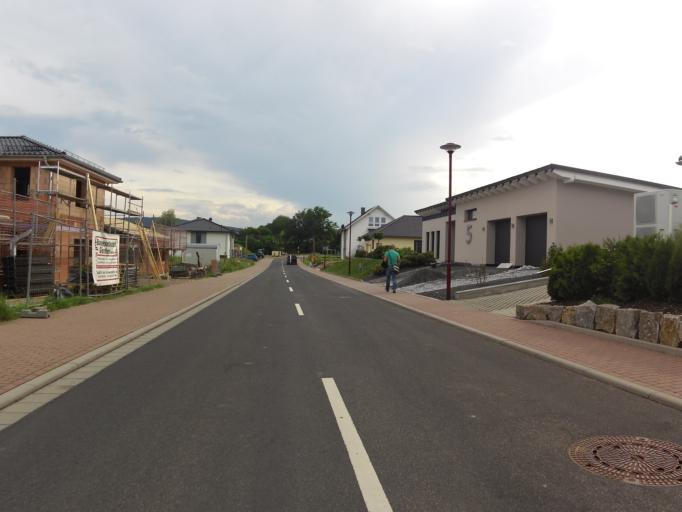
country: DE
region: Thuringia
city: Bad Salzungen
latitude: 50.8045
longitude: 10.2363
